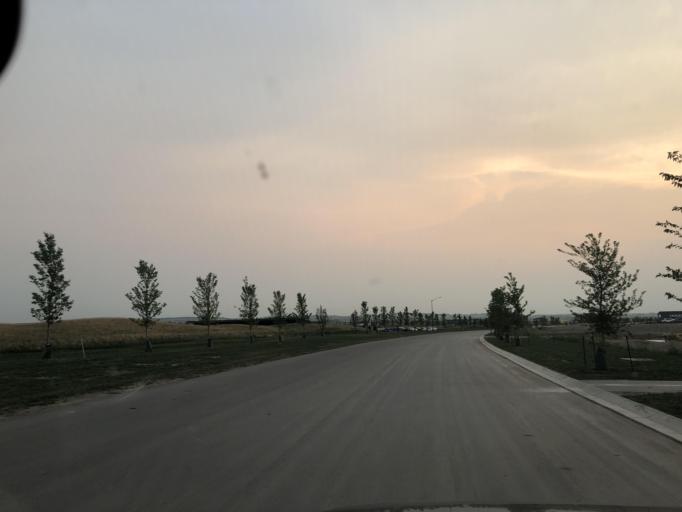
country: CA
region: Alberta
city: Cochrane
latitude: 51.1198
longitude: -114.3814
